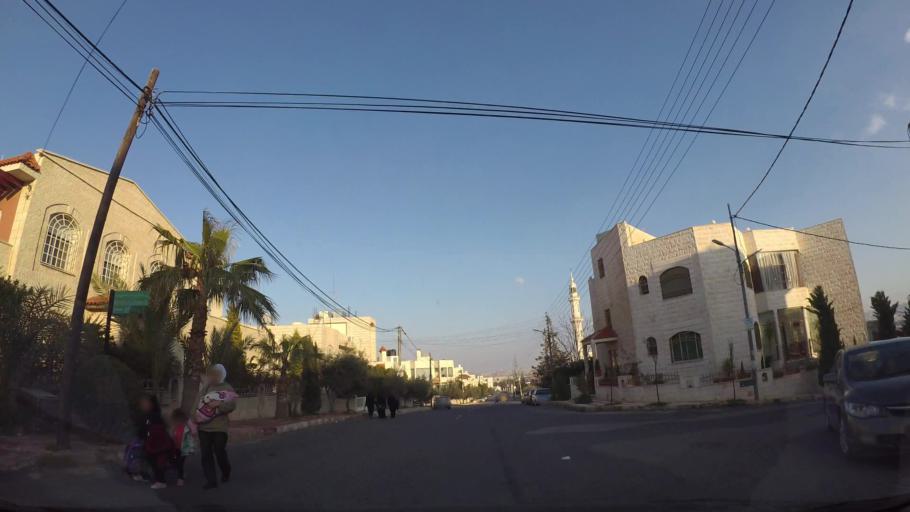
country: JO
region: Amman
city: Amman
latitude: 31.9852
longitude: 35.9623
